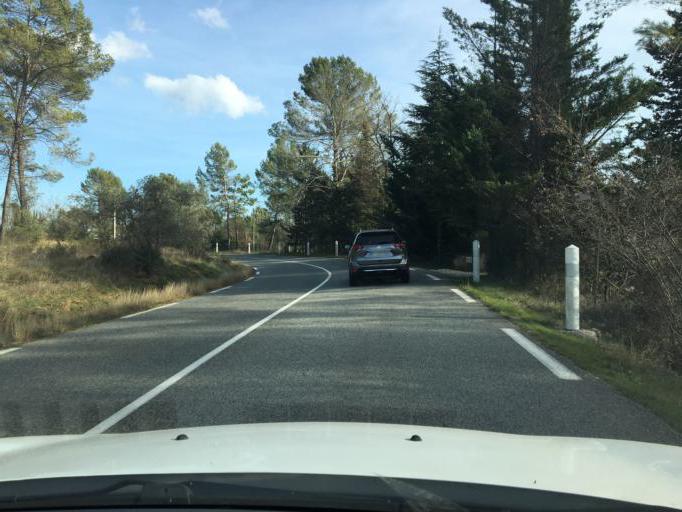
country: FR
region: Provence-Alpes-Cote d'Azur
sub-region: Departement du Var
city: Saint-Paul-en-Foret
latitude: 43.5893
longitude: 6.6794
